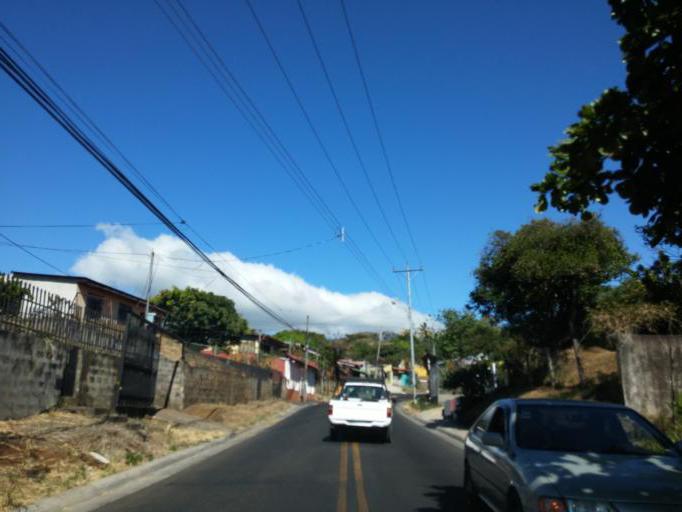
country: CR
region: Alajuela
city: Alajuela
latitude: 10.0197
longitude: -84.1857
